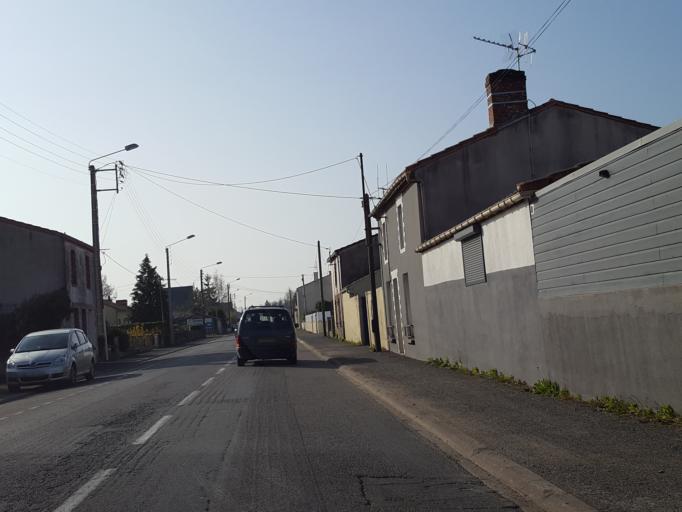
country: FR
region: Pays de la Loire
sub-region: Departement de la Loire-Atlantique
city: Geneston
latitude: 47.0602
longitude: -1.5152
